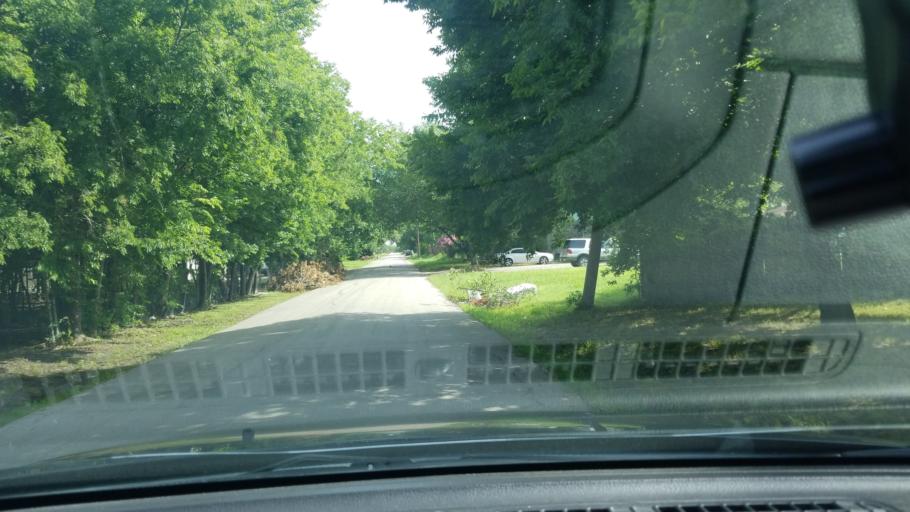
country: US
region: Texas
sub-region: Dallas County
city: Balch Springs
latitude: 32.7645
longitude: -96.6632
